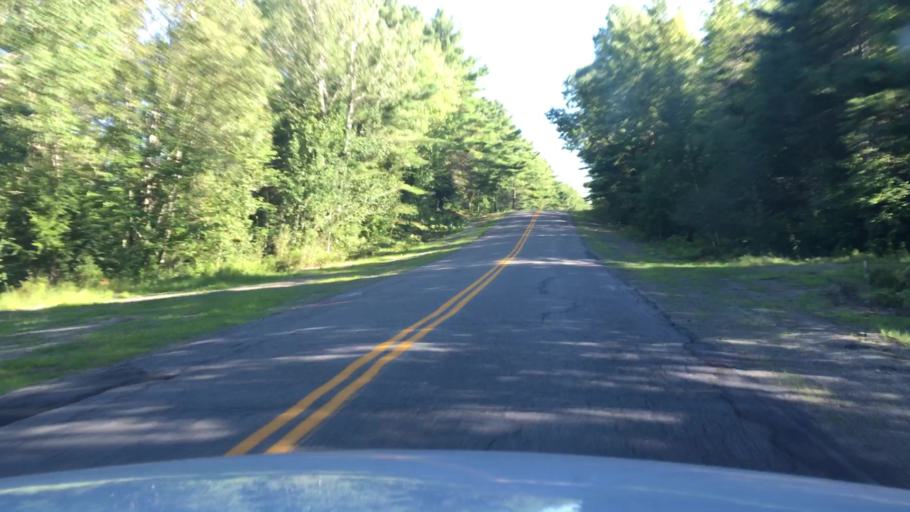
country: US
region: Maine
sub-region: Penobscot County
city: Enfield
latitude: 45.2307
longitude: -68.5805
